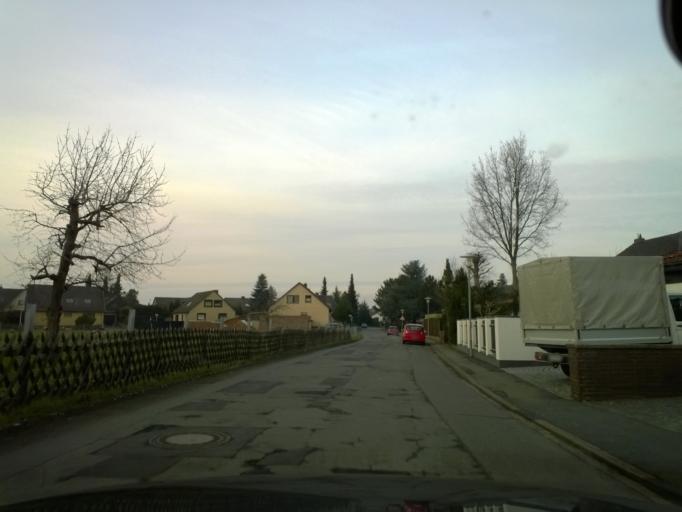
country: DE
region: Lower Saxony
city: Hildesheim
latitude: 52.1289
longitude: 9.9485
